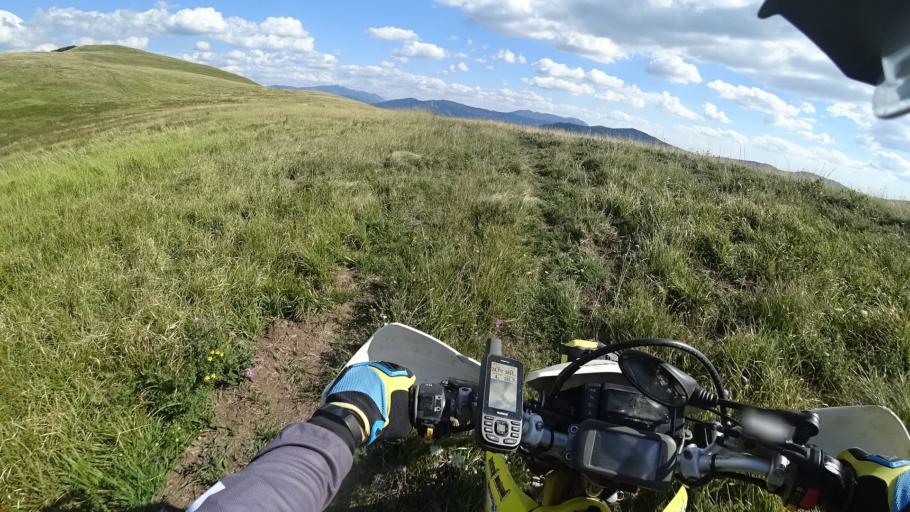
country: HR
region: Zadarska
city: Gracac
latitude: 44.3743
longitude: 16.0527
